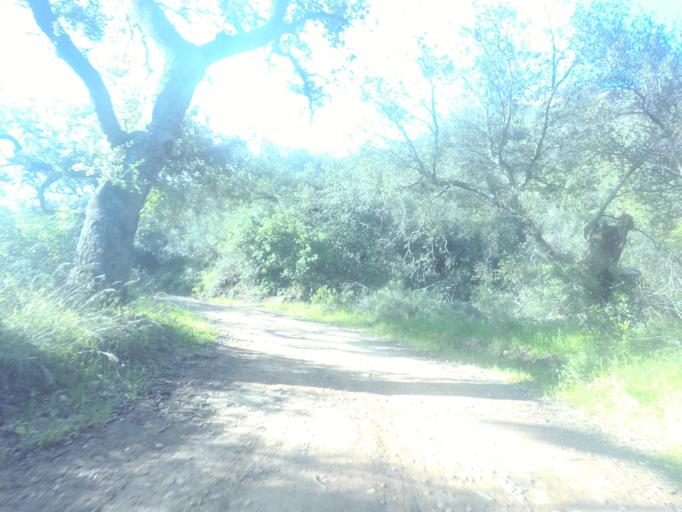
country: US
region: California
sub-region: Orange County
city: Foothill Ranch
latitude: 33.8024
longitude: -117.6578
